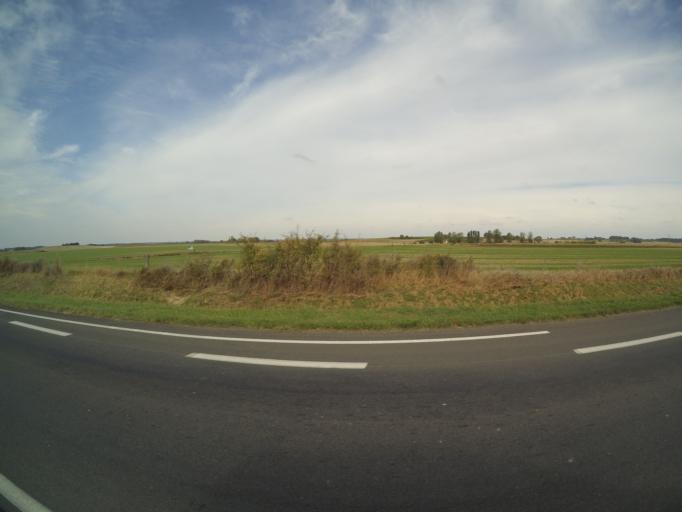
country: FR
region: Pays de la Loire
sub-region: Departement de Maine-et-Loire
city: Doue-la-Fontaine
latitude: 47.1969
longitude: -0.2474
